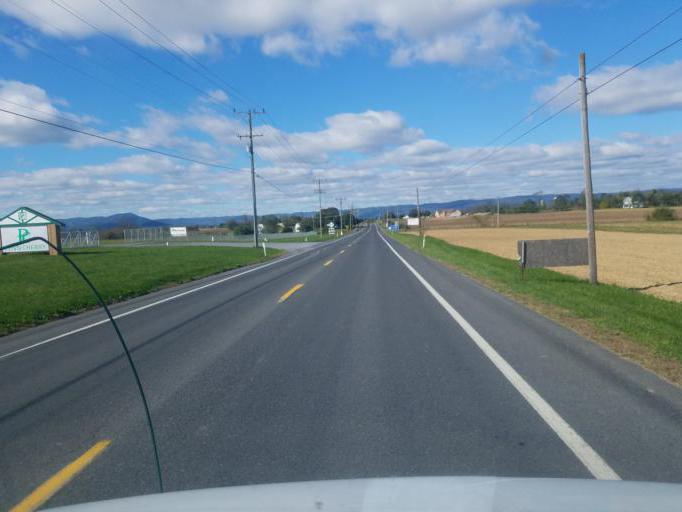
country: US
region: Pennsylvania
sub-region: Franklin County
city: Greencastle
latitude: 39.8049
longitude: -77.8162
